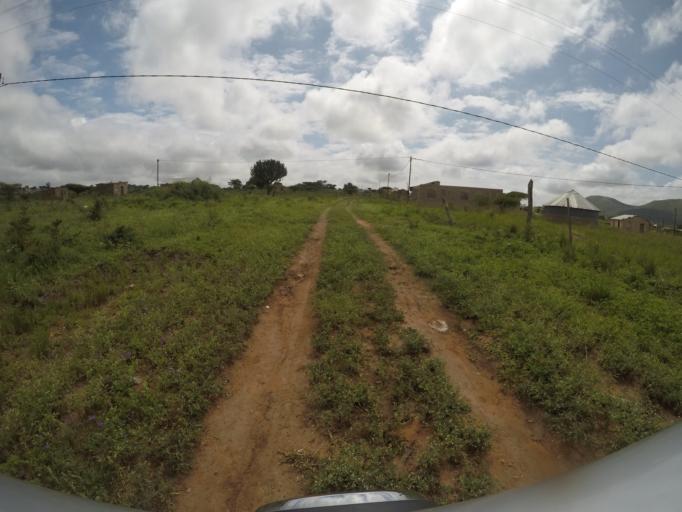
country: ZA
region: KwaZulu-Natal
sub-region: uThungulu District Municipality
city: Empangeni
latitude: -28.5849
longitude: 31.8483
